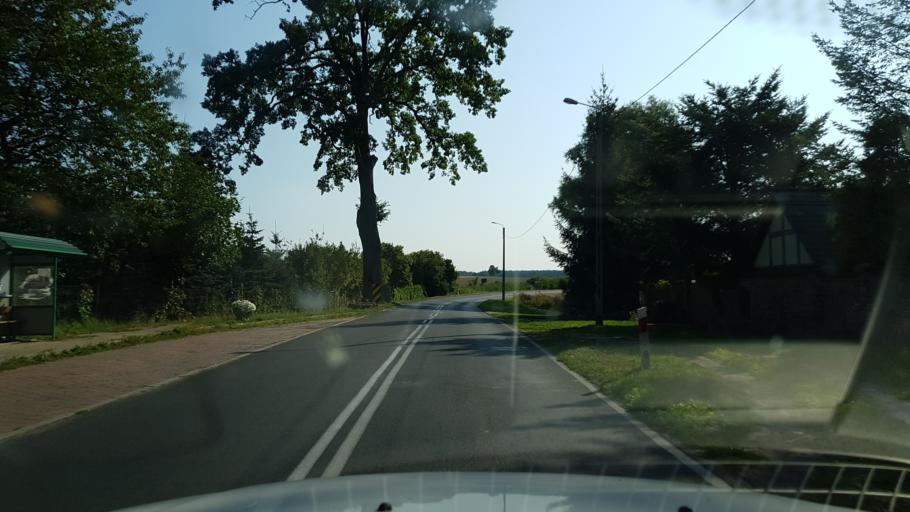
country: PL
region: West Pomeranian Voivodeship
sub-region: Powiat lobeski
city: Resko
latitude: 53.7751
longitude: 15.4302
